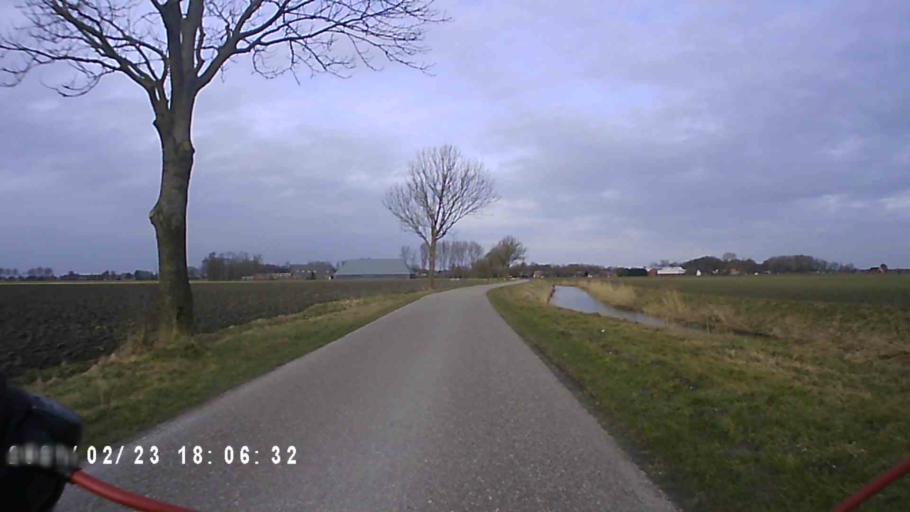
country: NL
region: Groningen
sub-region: Gemeente Bedum
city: Bedum
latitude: 53.3962
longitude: 6.6019
